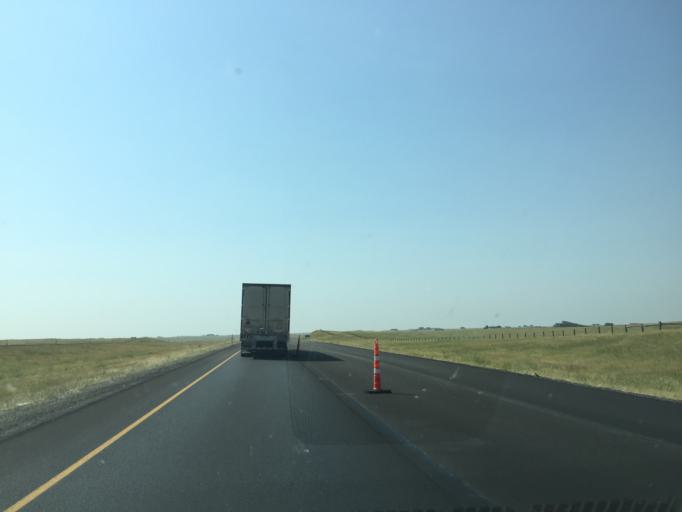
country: US
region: Wyoming
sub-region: Laramie County
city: Ranchettes
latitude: 41.3174
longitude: -104.8599
